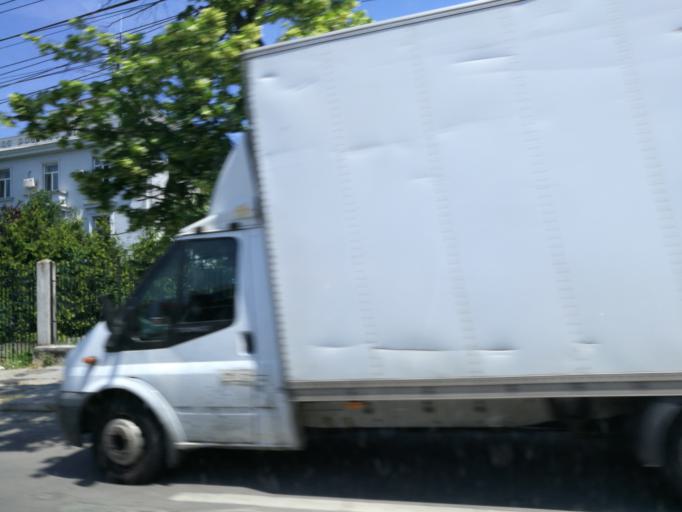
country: RO
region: Constanta
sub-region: Municipiul Constanta
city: Constanta
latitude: 44.1909
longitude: 28.6508
